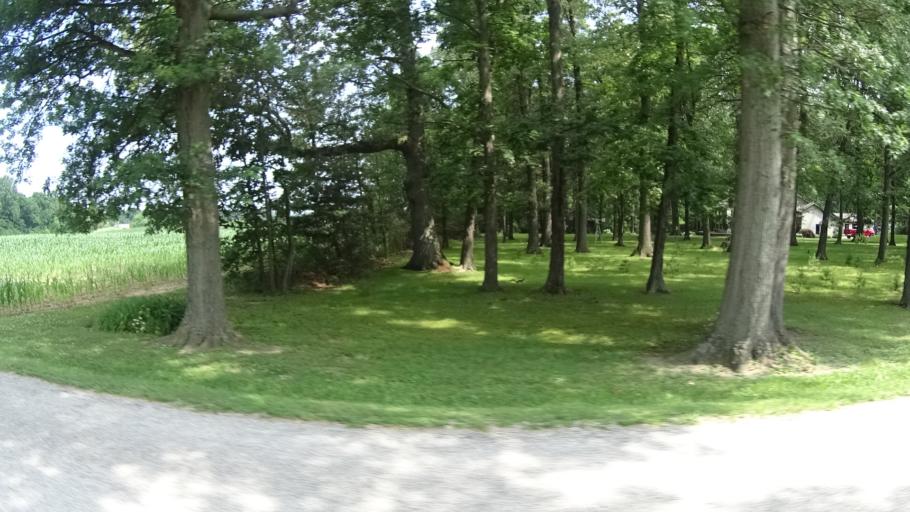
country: US
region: Ohio
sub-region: Lorain County
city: Vermilion
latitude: 41.3834
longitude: -82.4100
